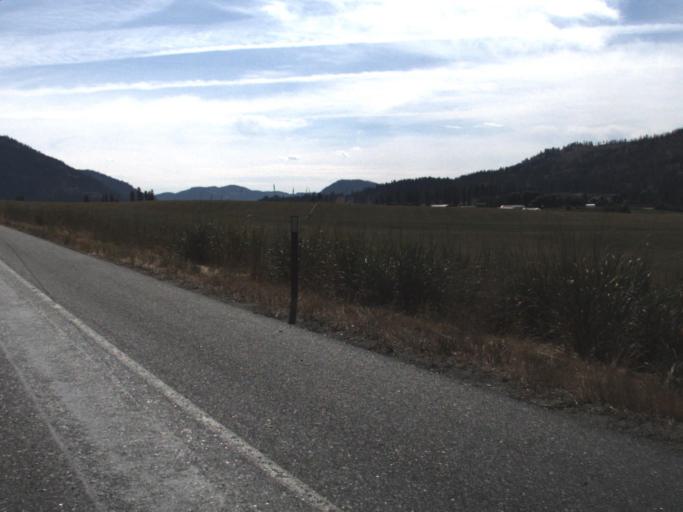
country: US
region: Washington
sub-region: Stevens County
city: Colville
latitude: 48.4375
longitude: -117.8644
